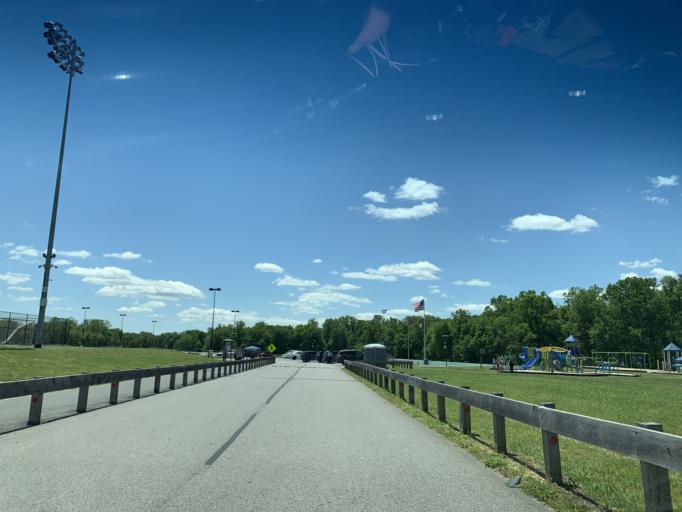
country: US
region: Pennsylvania
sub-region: Chester County
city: Oxford
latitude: 39.7003
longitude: -75.9740
